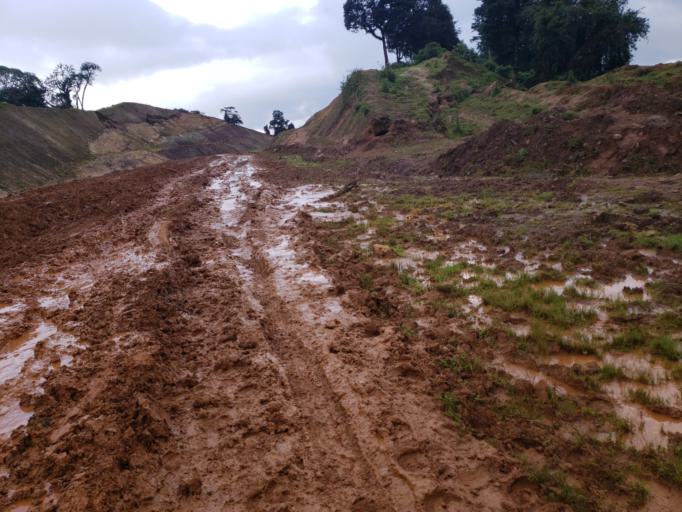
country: ET
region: Oromiya
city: Dodola
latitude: 6.6683
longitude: 39.3661
